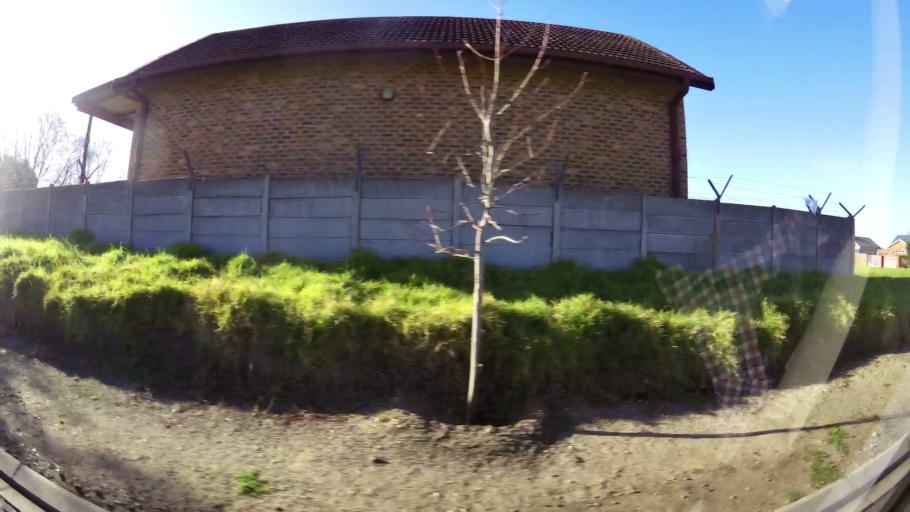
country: ZA
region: Western Cape
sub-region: Eden District Municipality
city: George
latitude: -33.9573
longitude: 22.4450
